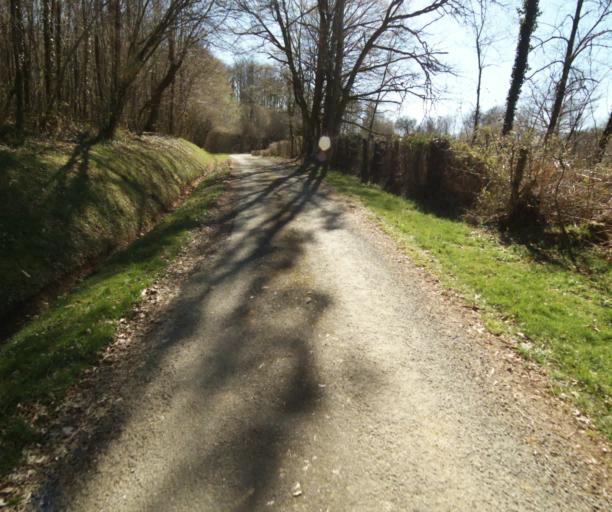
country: FR
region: Limousin
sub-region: Departement de la Correze
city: Saint-Clement
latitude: 45.3883
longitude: 1.6628
